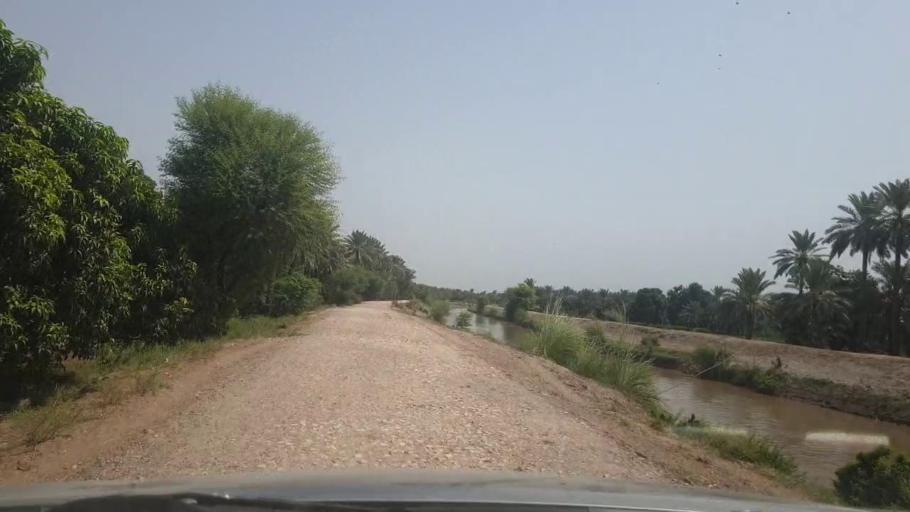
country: PK
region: Sindh
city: Pano Aqil
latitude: 27.8859
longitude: 69.1305
